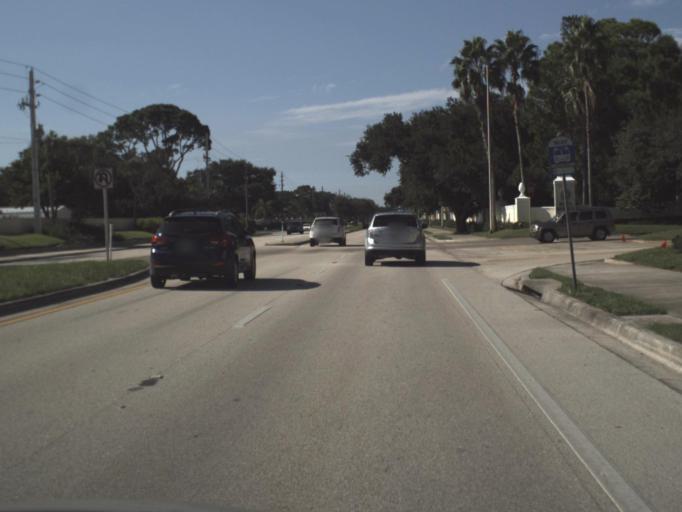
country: US
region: Florida
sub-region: Sarasota County
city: Englewood
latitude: 26.9956
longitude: -82.3724
